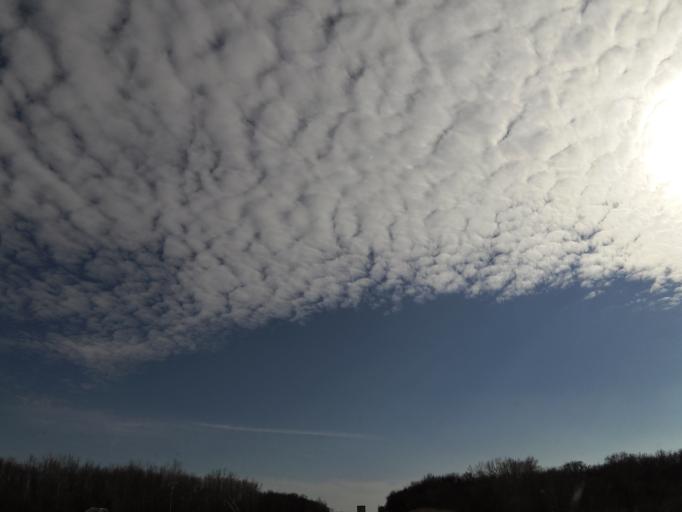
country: US
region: Minnesota
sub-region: Steele County
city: Medford
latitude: 44.1959
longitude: -93.2552
